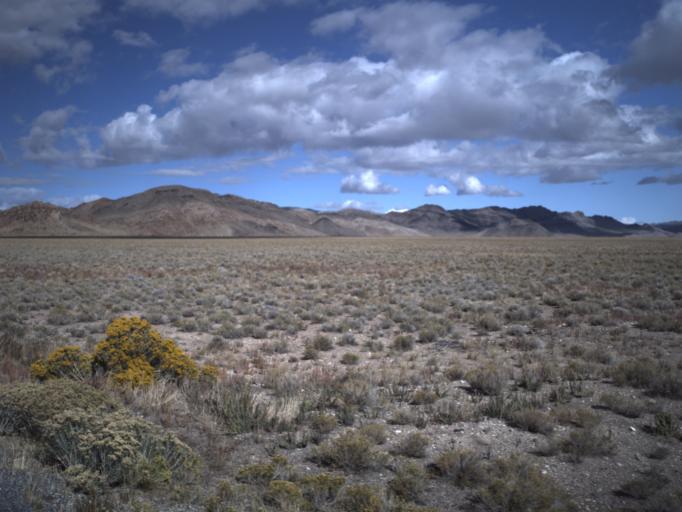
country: US
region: Utah
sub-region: Beaver County
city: Milford
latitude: 38.5700
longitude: -113.7838
